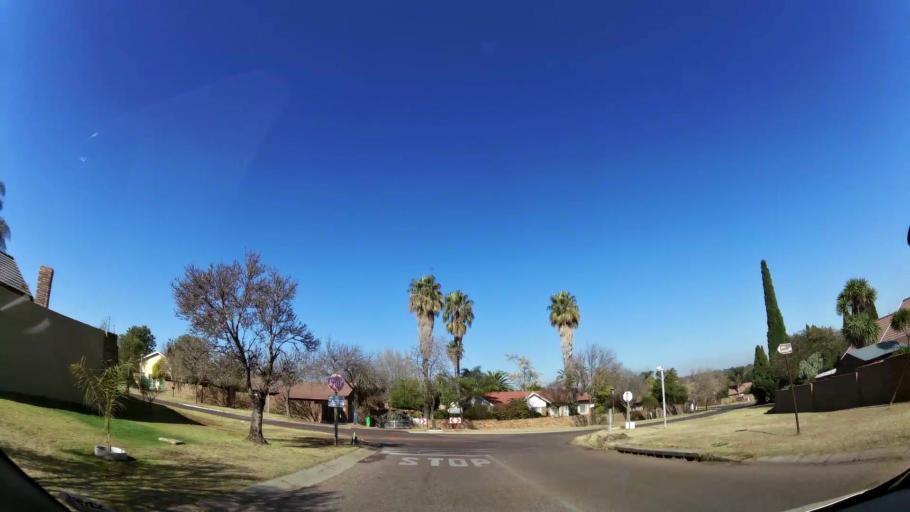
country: ZA
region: Mpumalanga
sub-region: Nkangala District Municipality
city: Witbank
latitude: -25.8887
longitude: 29.2481
